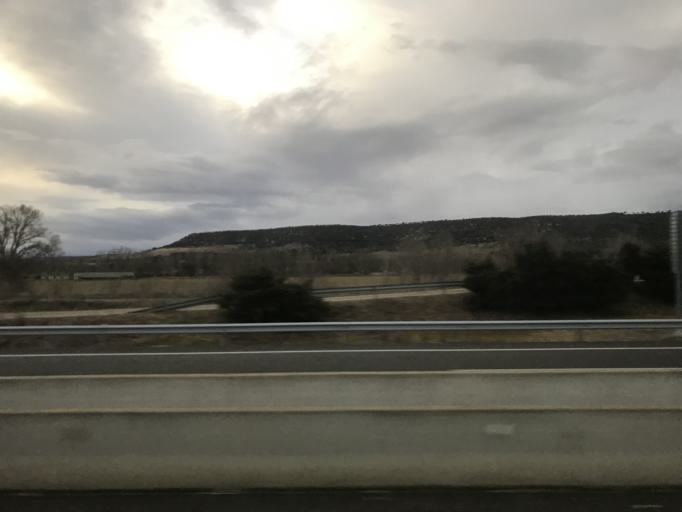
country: ES
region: Castille and Leon
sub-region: Provincia de Palencia
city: Quintana del Puente
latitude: 42.0777
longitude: -4.2114
